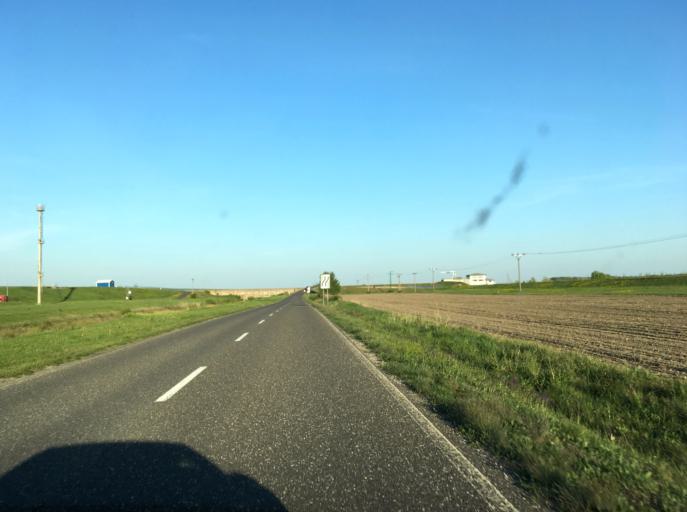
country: SK
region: Trnavsky
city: Samorin
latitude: 47.9929
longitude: 17.3472
